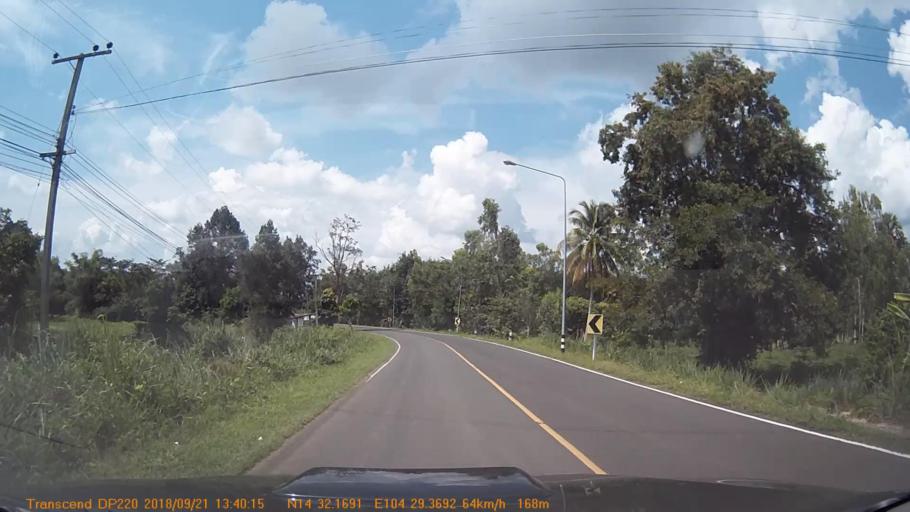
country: TH
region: Sisaket
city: Khun Han
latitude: 14.5364
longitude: 104.4895
